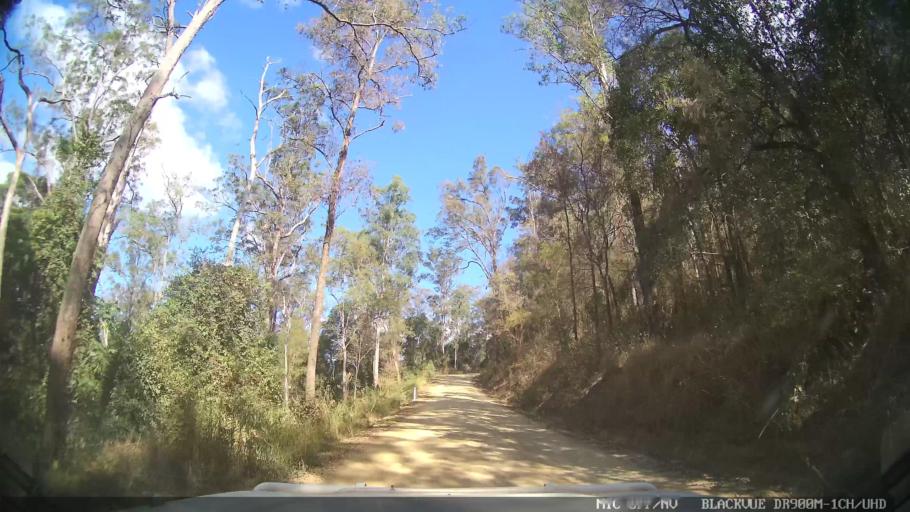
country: AU
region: Queensland
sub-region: Moreton Bay
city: Woodford
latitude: -26.6679
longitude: 152.6353
